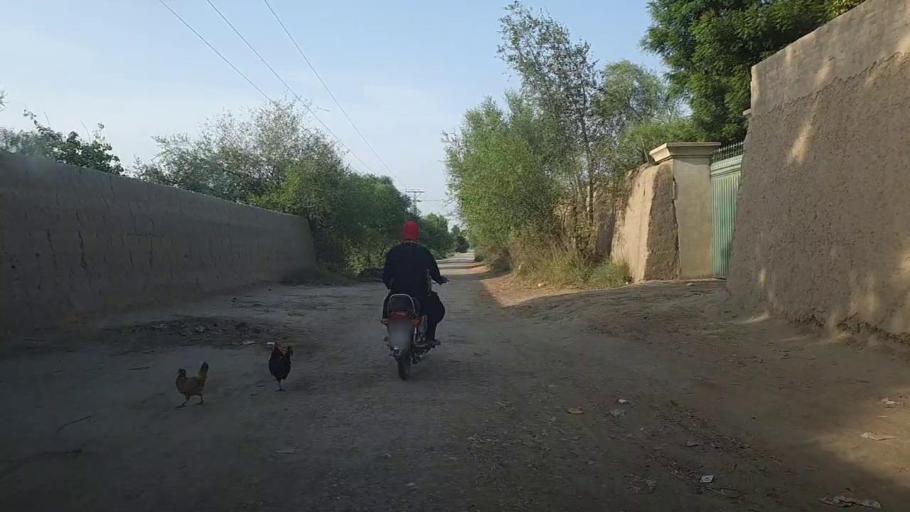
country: PK
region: Sindh
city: Ubauro
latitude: 28.3271
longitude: 69.7970
